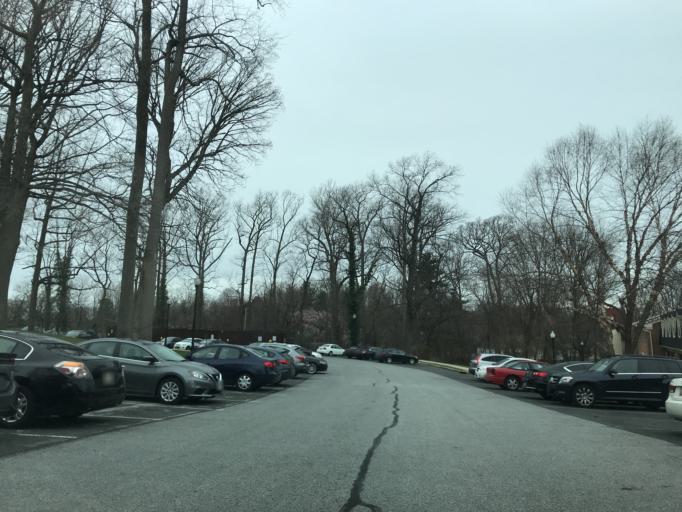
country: US
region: Maryland
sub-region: Baltimore County
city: Towson
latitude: 39.3957
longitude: -76.5867
